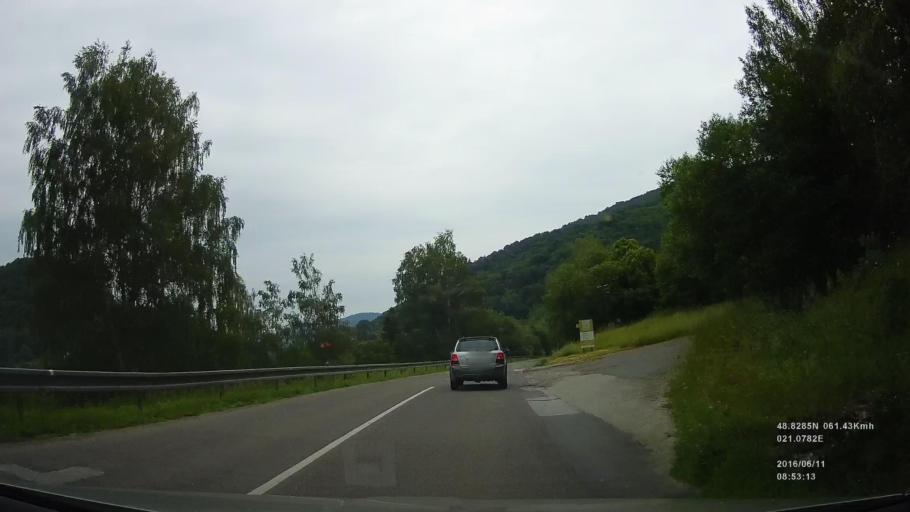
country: SK
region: Kosicky
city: Gelnica
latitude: 48.8236
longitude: 21.0808
